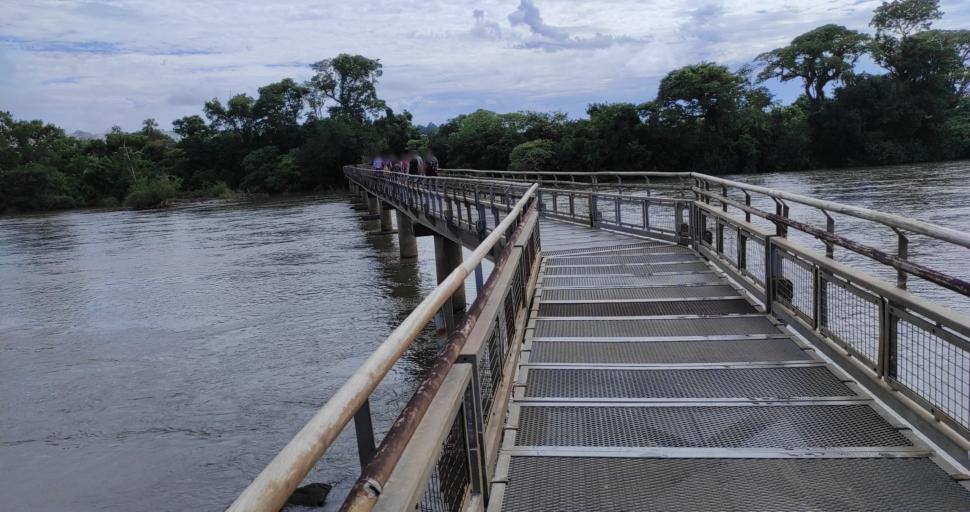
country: AR
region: Misiones
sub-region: Departamento de Iguazu
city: Puerto Iguazu
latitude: -25.6977
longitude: -54.4400
